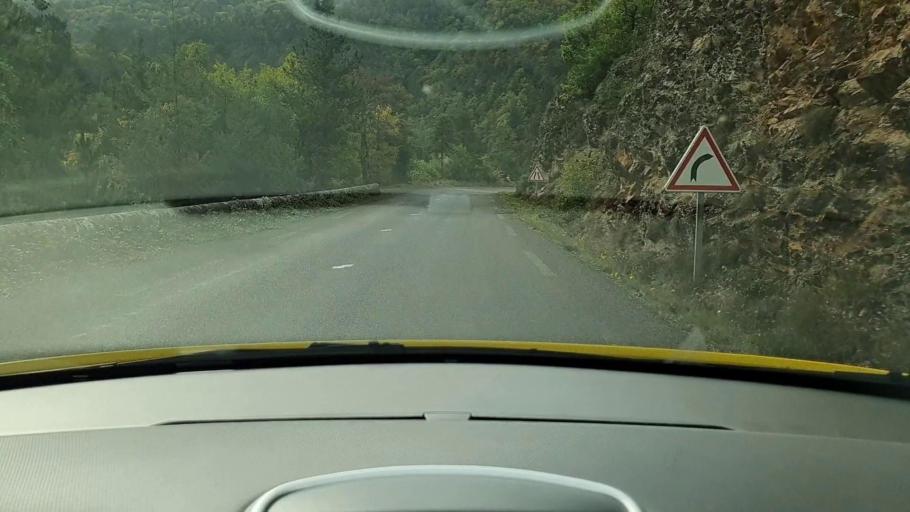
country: FR
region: Languedoc-Roussillon
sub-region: Departement de la Lozere
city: Meyrueis
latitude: 44.1106
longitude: 3.4306
